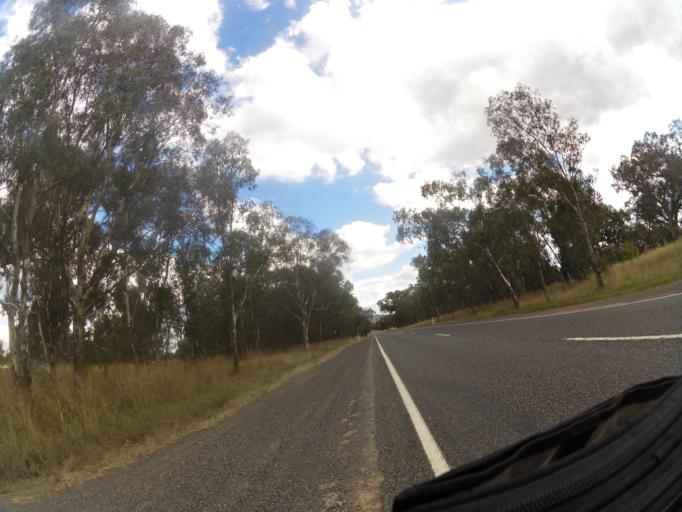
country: AU
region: Victoria
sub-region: Mansfield
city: Mansfield
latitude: -37.0328
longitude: 146.0922
